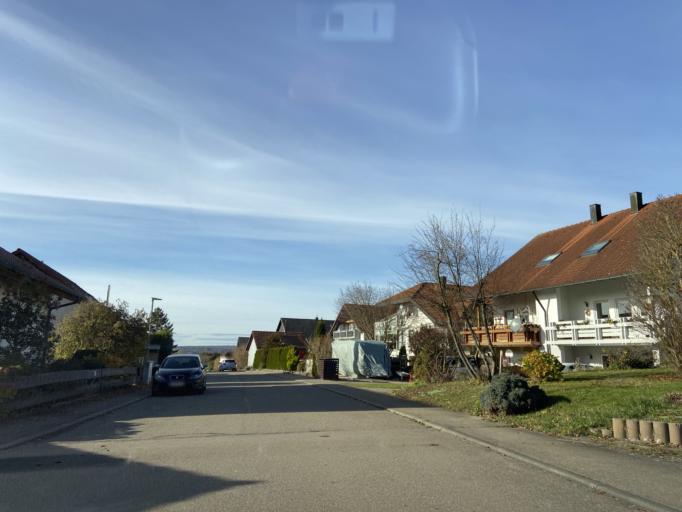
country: DE
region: Baden-Wuerttemberg
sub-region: Tuebingen Region
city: Sigmaringen
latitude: 48.0893
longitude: 9.2390
